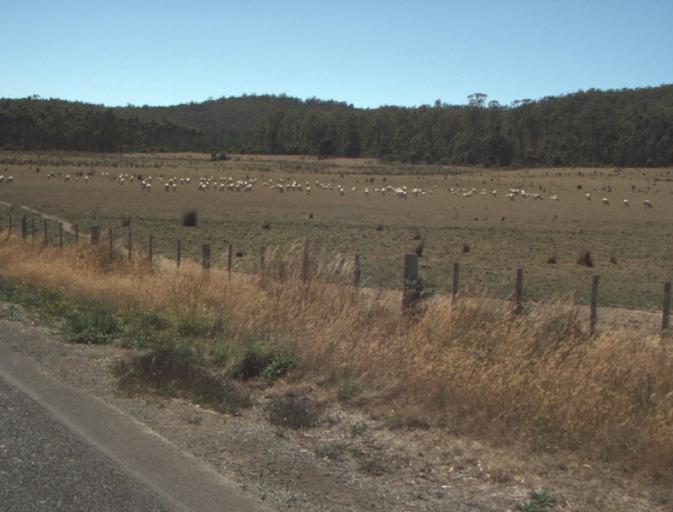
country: AU
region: Tasmania
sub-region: Launceston
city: Newstead
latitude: -41.3367
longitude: 147.3050
